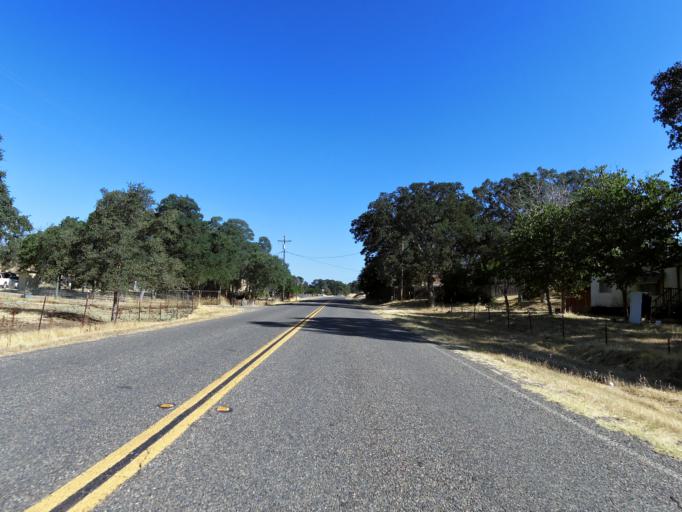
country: US
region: California
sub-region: Mariposa County
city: Mariposa
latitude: 37.4328
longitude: -120.0990
